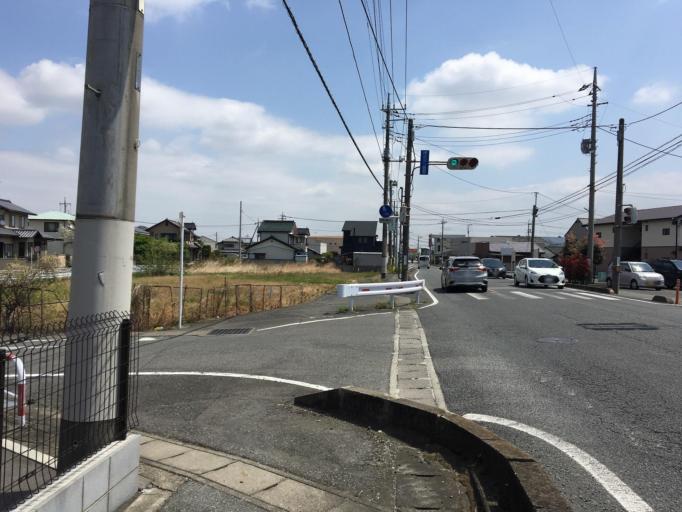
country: JP
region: Gunma
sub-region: Sawa-gun
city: Tamamura
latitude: 36.3021
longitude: 139.1278
